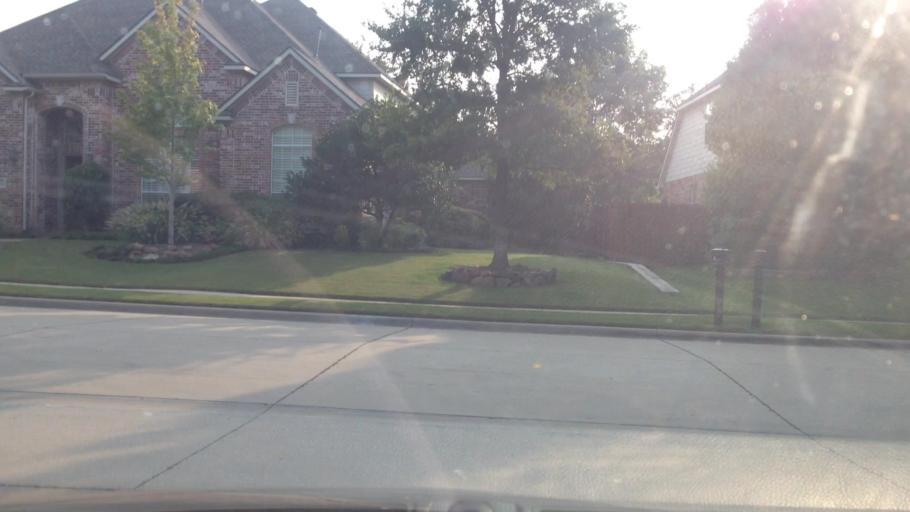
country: US
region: Texas
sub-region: Collin County
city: Frisco
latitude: 33.1270
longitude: -96.8401
